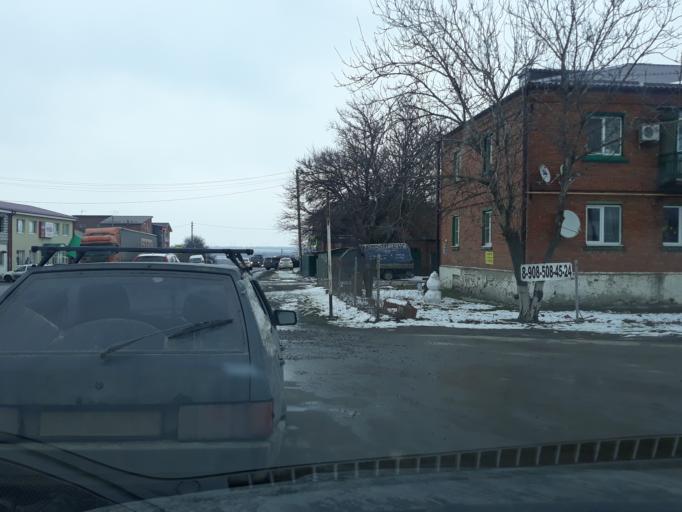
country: RU
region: Rostov
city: Krym
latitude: 47.2777
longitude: 39.5123
